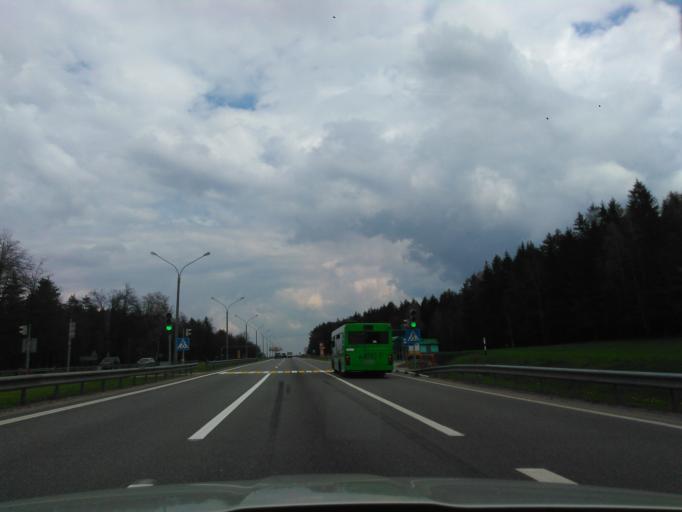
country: BY
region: Minsk
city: Korolev Stan
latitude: 53.9798
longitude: 27.7761
